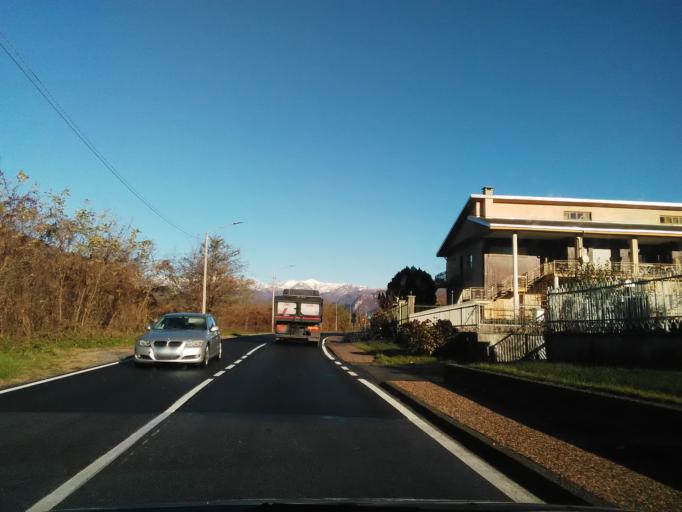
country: IT
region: Piedmont
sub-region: Provincia di Vercelli
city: Quarona
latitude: 45.7490
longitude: 8.2649
